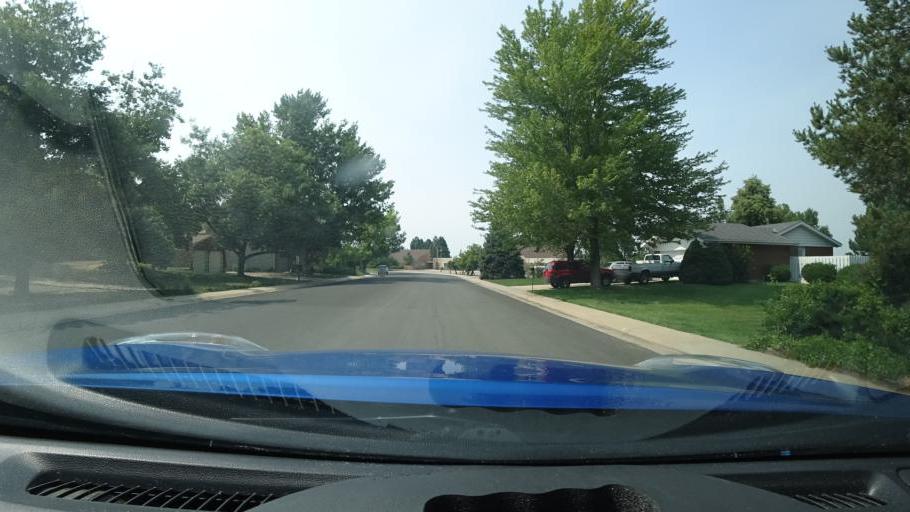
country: US
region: Colorado
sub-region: Adams County
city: Aurora
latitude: 39.6730
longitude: -104.8537
